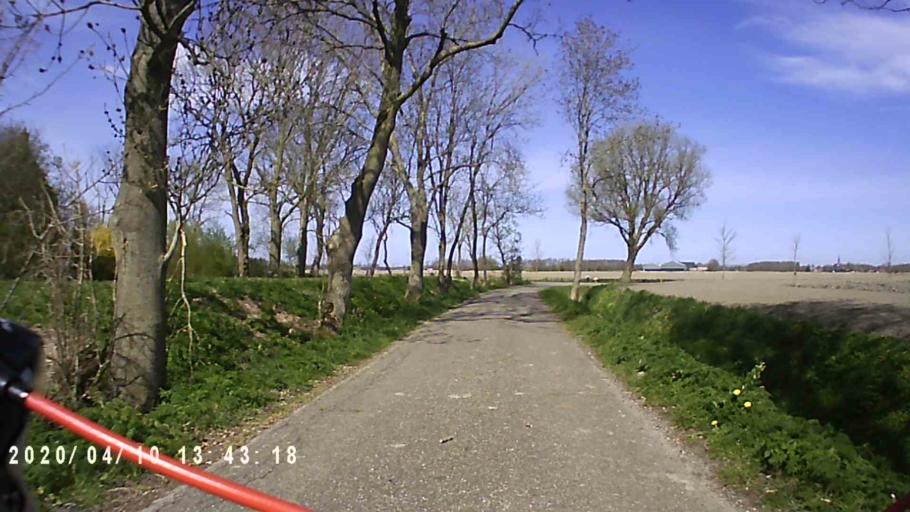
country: NL
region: Groningen
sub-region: Gemeente De Marne
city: Ulrum
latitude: 53.3740
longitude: 6.3831
